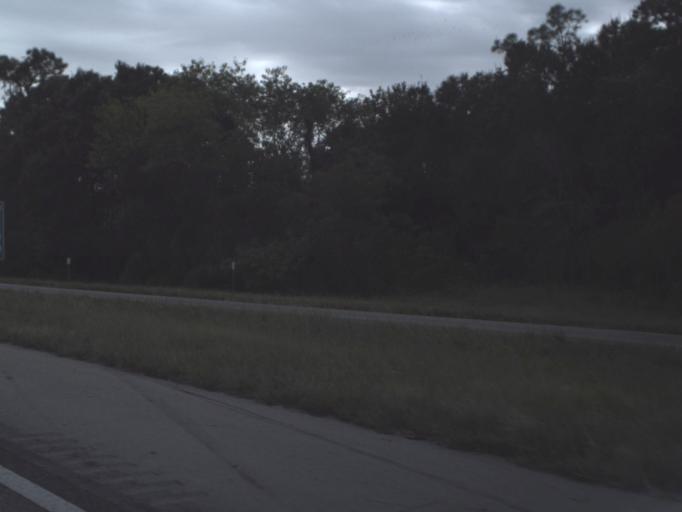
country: US
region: Florida
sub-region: Lee County
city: Tice
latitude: 26.6534
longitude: -81.7996
